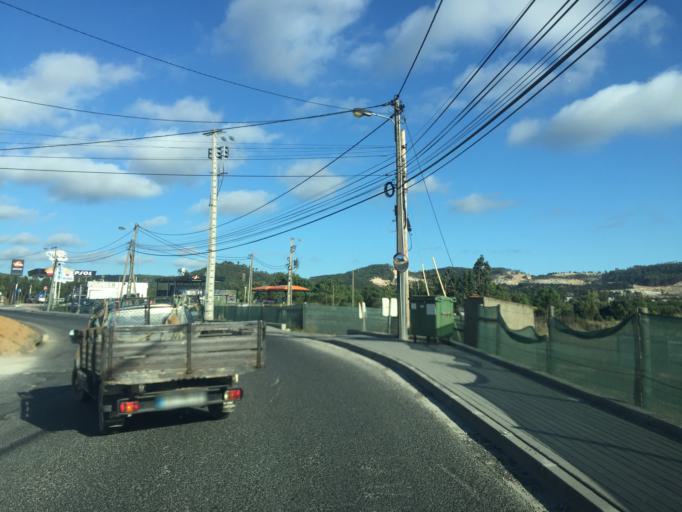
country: PT
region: Lisbon
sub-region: Torres Vedras
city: A dos Cunhados
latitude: 39.1460
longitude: -9.2835
